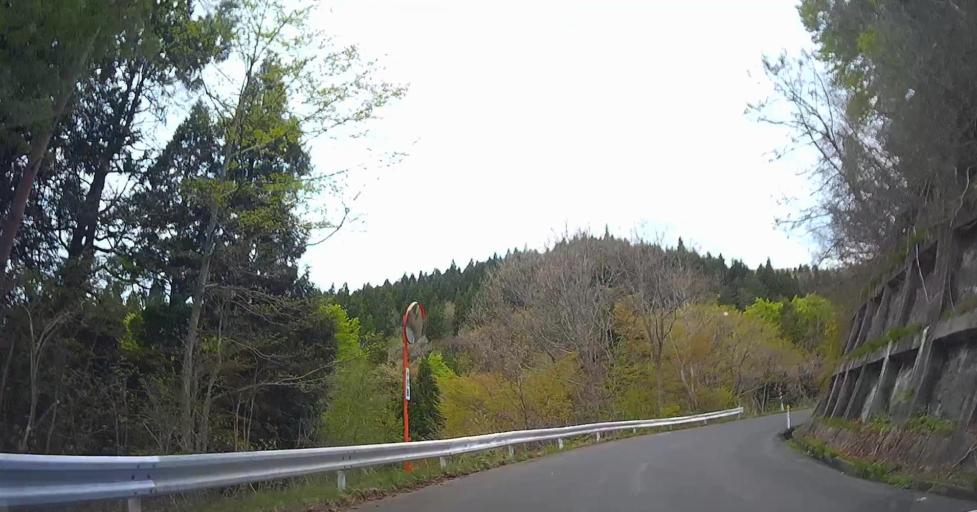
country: JP
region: Aomori
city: Goshogawara
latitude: 40.9049
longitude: 140.5170
